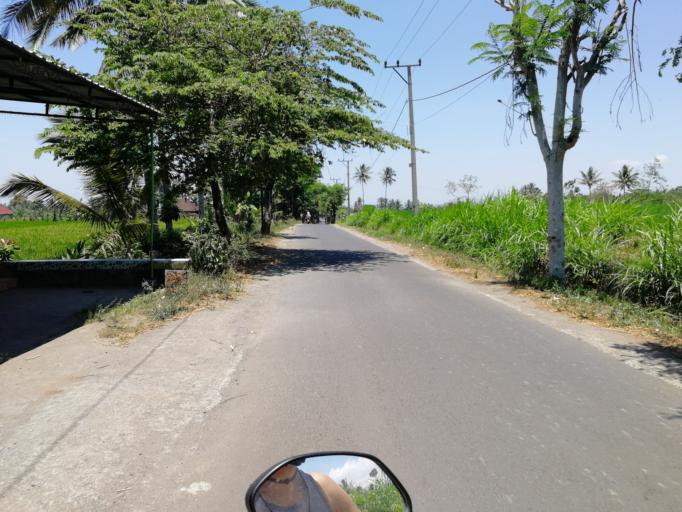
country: ID
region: West Nusa Tenggara
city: Tetebatu
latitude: -8.5566
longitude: 116.4194
